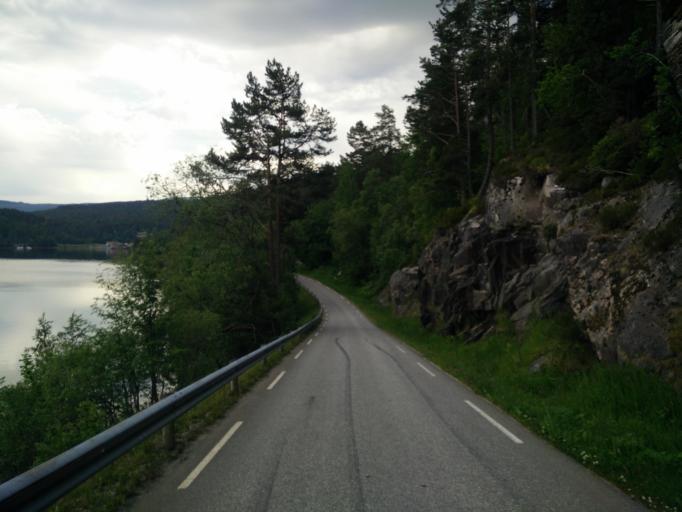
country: NO
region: More og Romsdal
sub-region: Kristiansund
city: Rensvik
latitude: 63.0285
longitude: 7.9540
